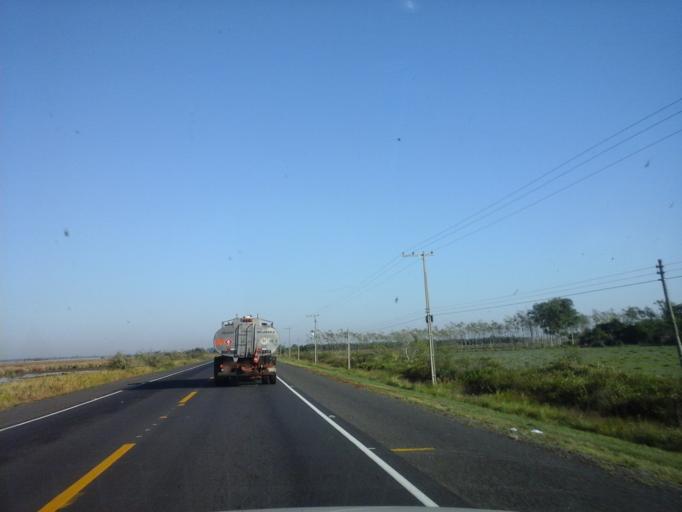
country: PY
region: Neembucu
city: Pilar
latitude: -26.8515
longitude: -58.2196
